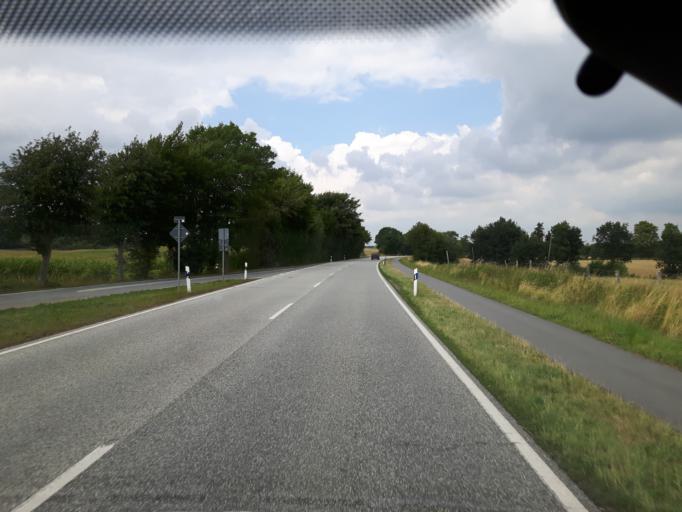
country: DE
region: Schleswig-Holstein
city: Holzbunge
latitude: 54.3678
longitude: 9.7031
